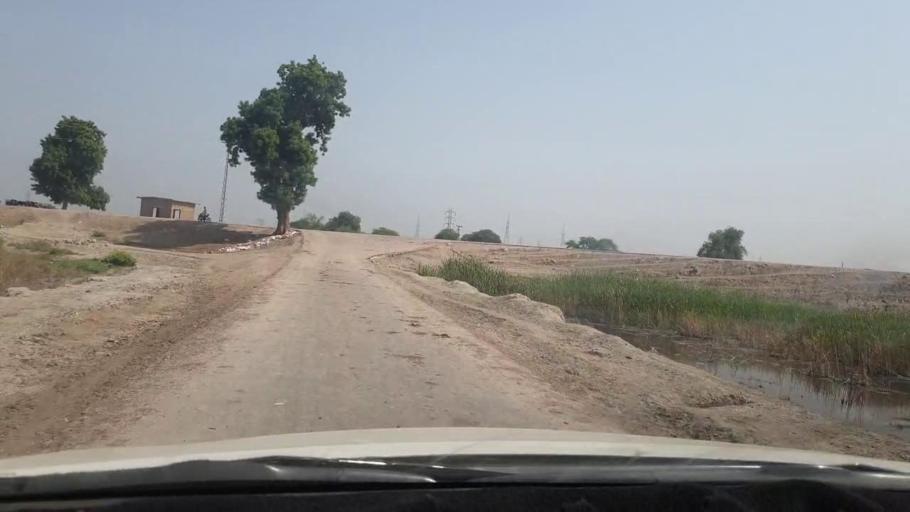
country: PK
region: Sindh
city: Rohri
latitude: 27.6378
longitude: 68.8841
